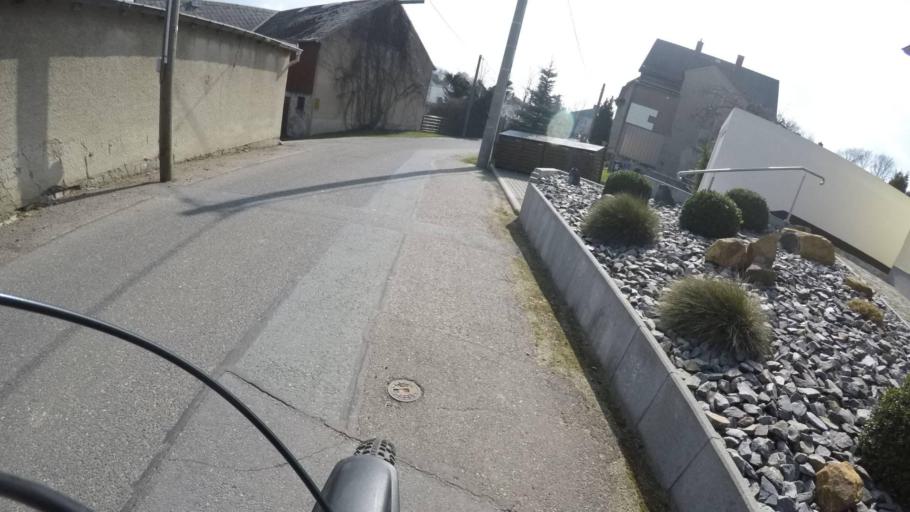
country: DE
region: Saxony
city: Limbach-Oberfrohna
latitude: 50.8653
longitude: 12.7374
